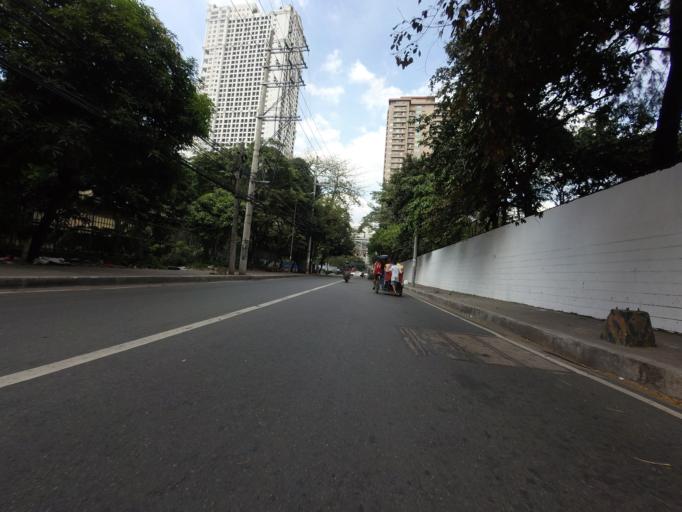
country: PH
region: Metro Manila
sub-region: City of Manila
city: Port Area
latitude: 14.5645
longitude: 120.9872
